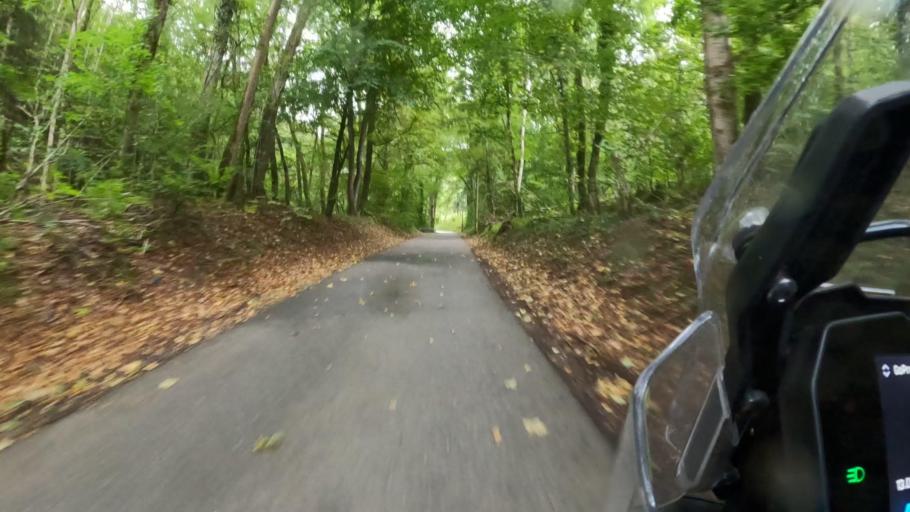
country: DE
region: Baden-Wuerttemberg
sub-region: Freiburg Region
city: Wutoschingen
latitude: 47.6756
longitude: 8.3835
